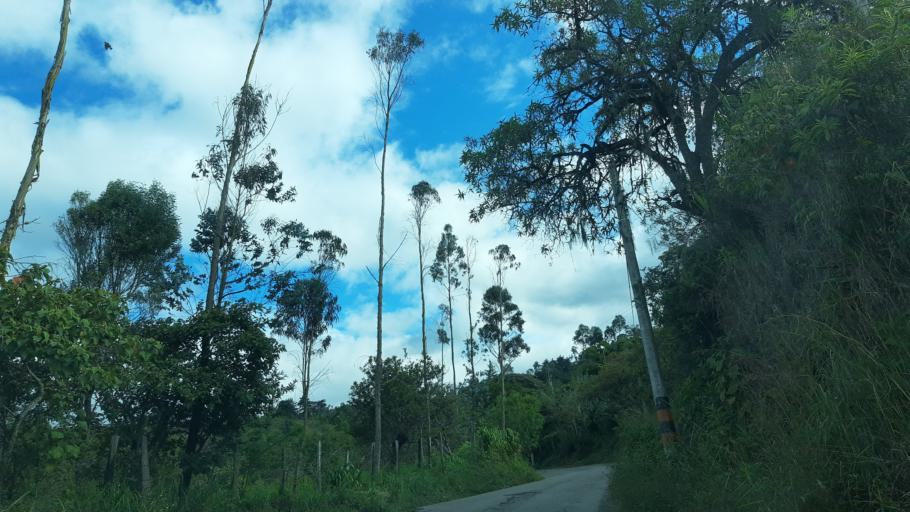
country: CO
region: Cundinamarca
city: Tenza
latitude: 5.0607
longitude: -73.4213
